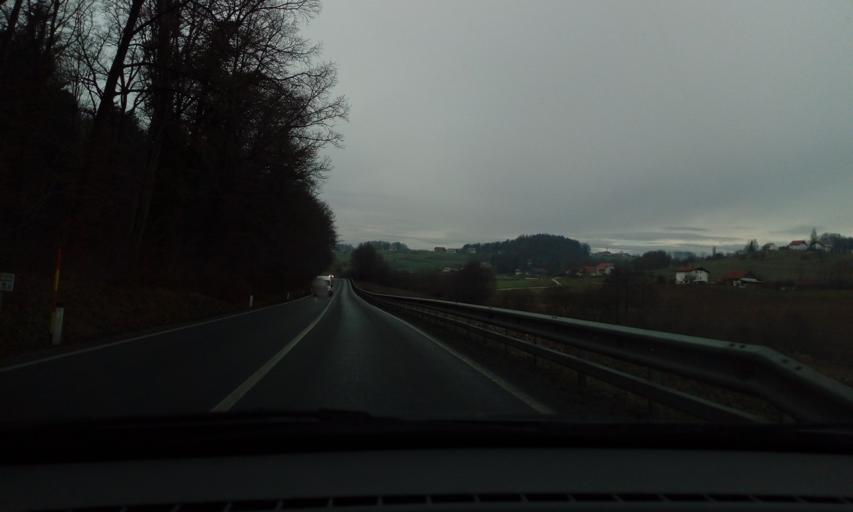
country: SI
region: Smarje pri Jelsah
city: Smarje pri Jelsah
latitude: 46.2300
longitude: 15.4998
